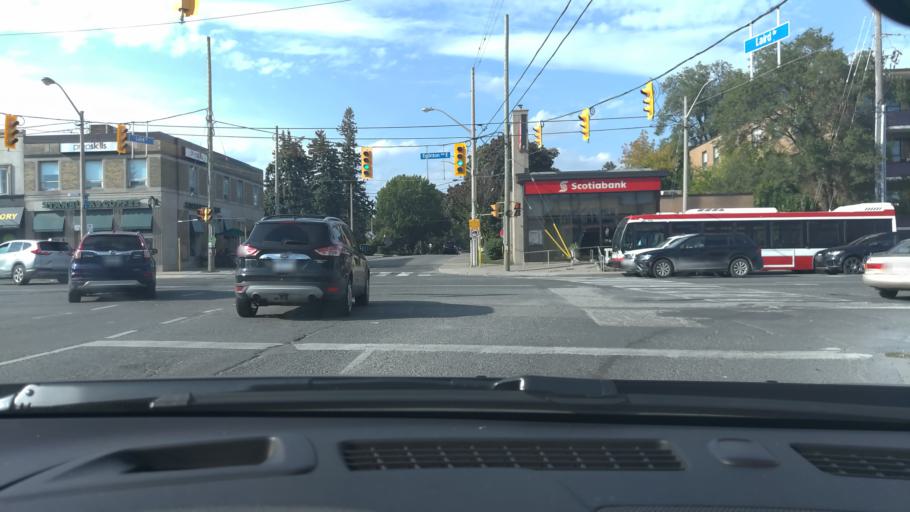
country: CA
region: Ontario
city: Toronto
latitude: 43.7134
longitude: -79.3646
